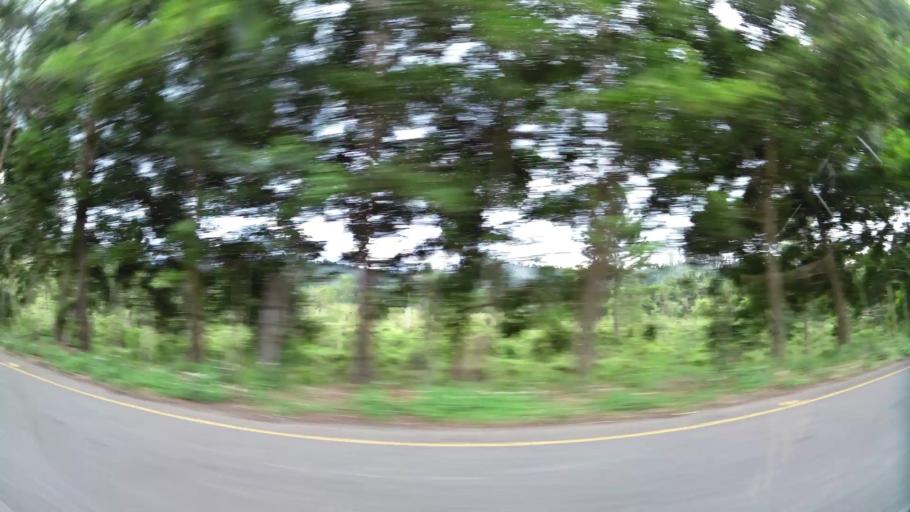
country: DO
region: San Cristobal
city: Villa Altagracia
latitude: 18.7240
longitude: -70.2320
